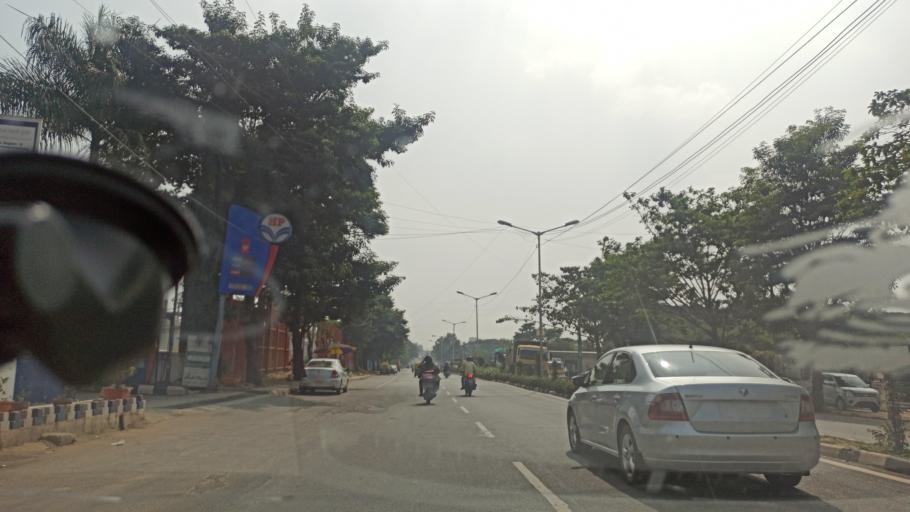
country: IN
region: Karnataka
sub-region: Bangalore Urban
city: Yelahanka
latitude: 13.0923
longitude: 77.5942
